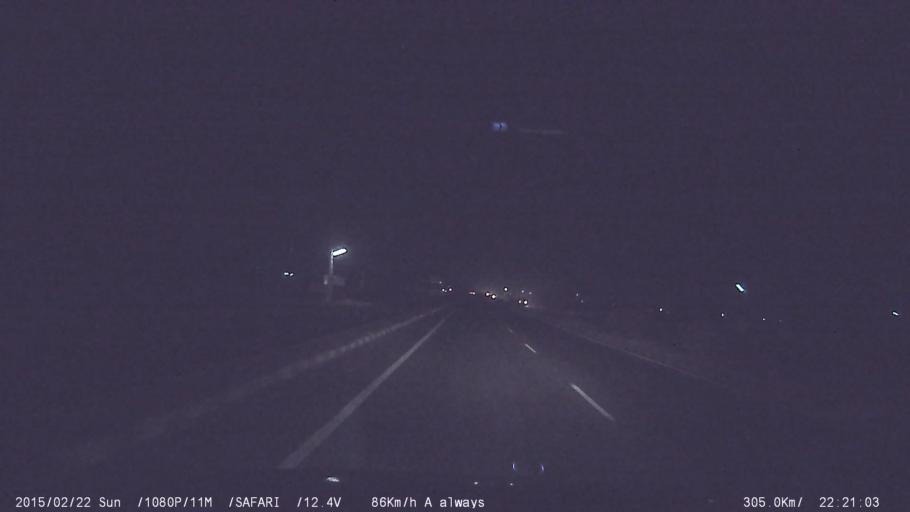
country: IN
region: Tamil Nadu
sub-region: Karur
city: Karur
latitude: 10.9975
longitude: 78.0669
